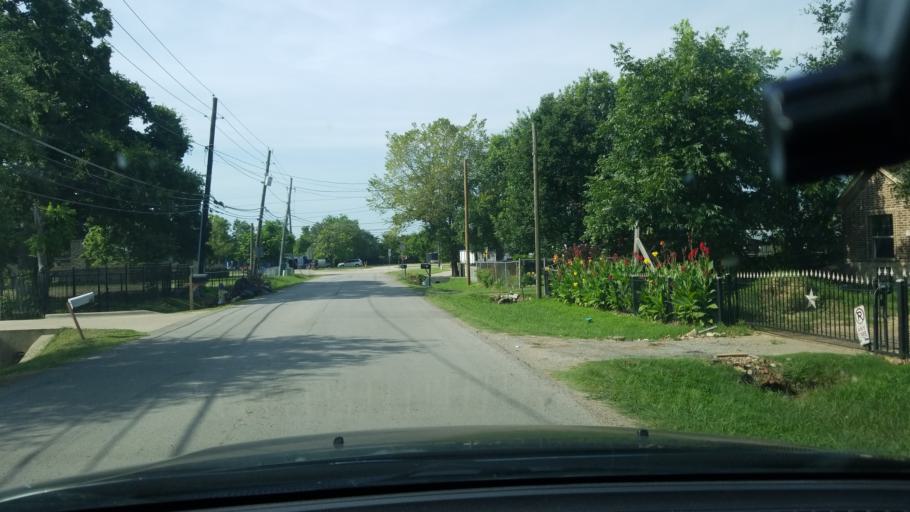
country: US
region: Texas
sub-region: Dallas County
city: Balch Springs
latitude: 32.7206
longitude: -96.6393
